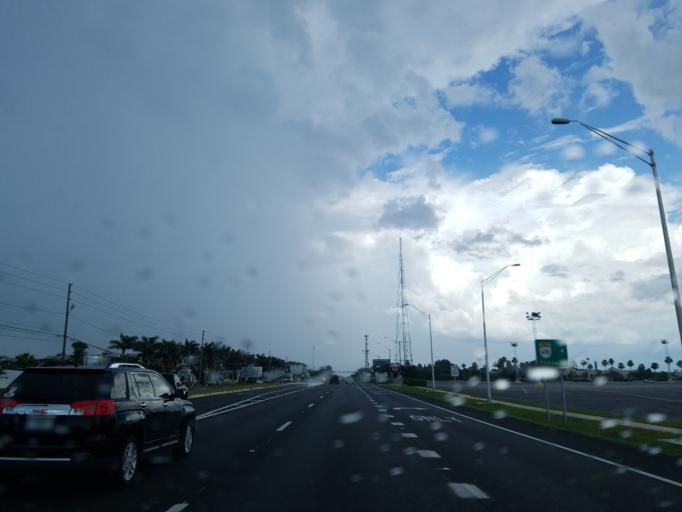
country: US
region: Florida
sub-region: Pinellas County
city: Gandy
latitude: 27.8654
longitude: -82.6305
